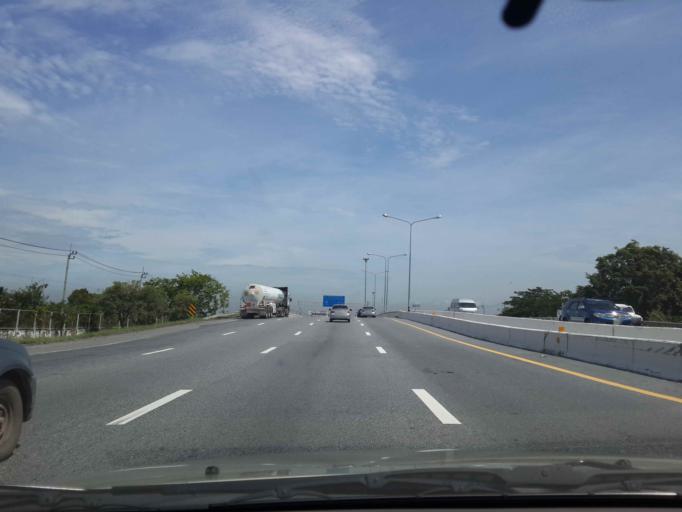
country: TH
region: Samut Prakan
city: Ban Khlong Bang Sao Thong
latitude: 13.6655
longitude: 100.8504
